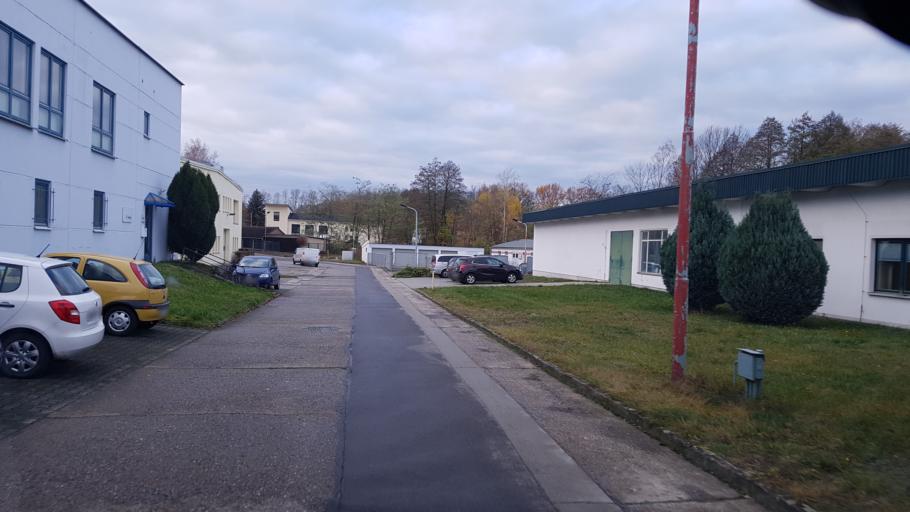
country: DE
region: Brandenburg
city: Ortrand
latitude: 51.3751
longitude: 13.7701
